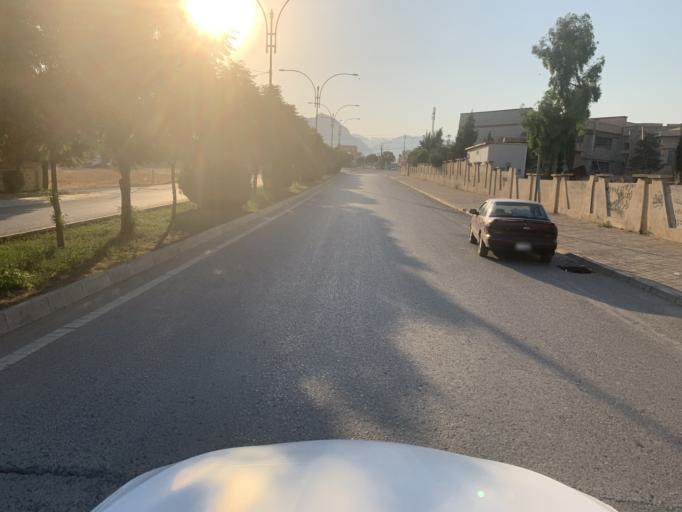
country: IQ
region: As Sulaymaniyah
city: Raniye
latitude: 36.2399
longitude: 44.8770
